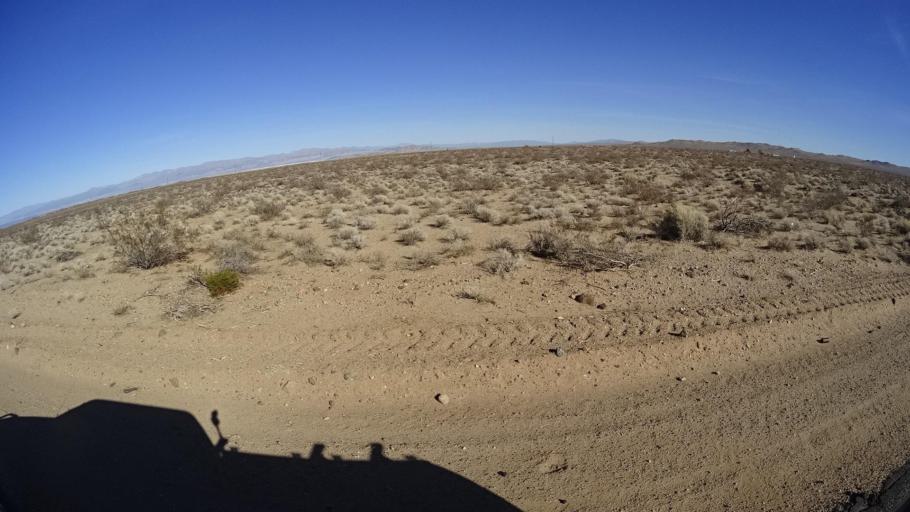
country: US
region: California
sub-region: Kern County
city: China Lake Acres
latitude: 35.5746
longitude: -117.7835
